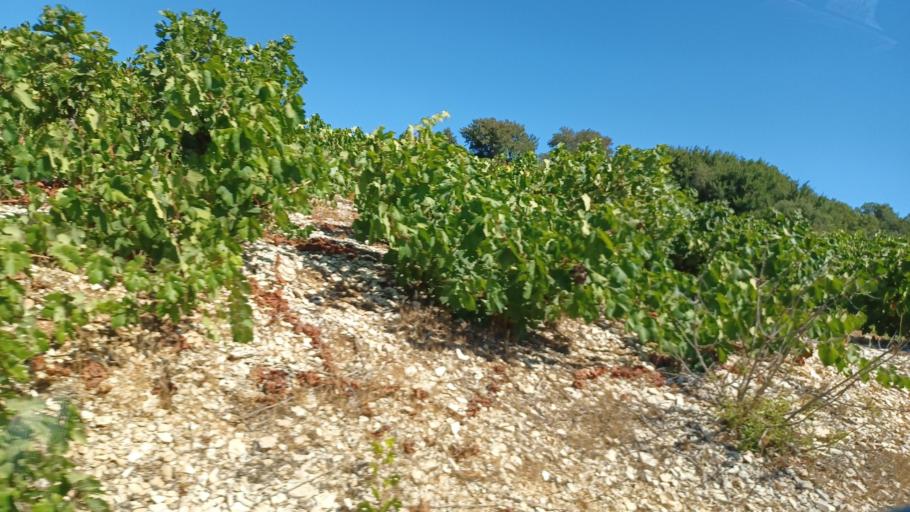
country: CY
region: Pafos
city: Mesogi
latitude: 34.9020
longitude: 32.6356
